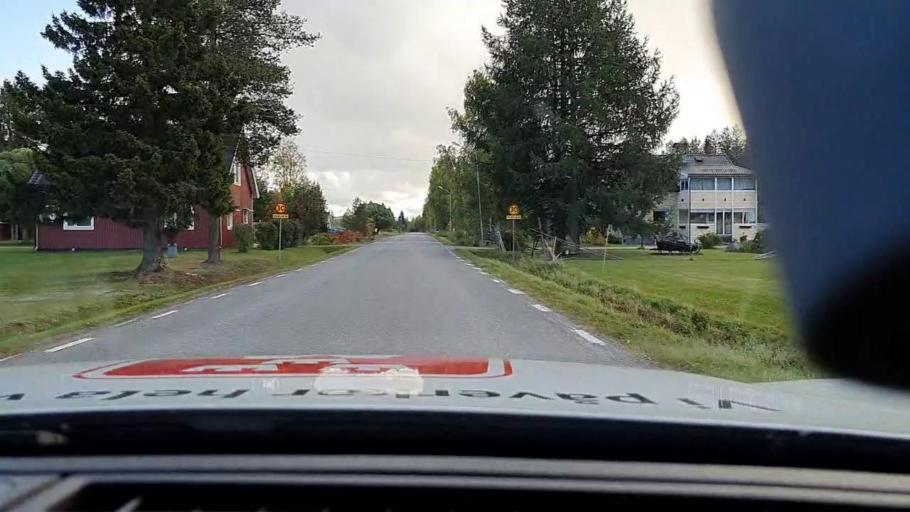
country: SE
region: Vaesterbotten
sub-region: Skelleftea Kommun
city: Langsele
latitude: 64.9512
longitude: 19.9253
